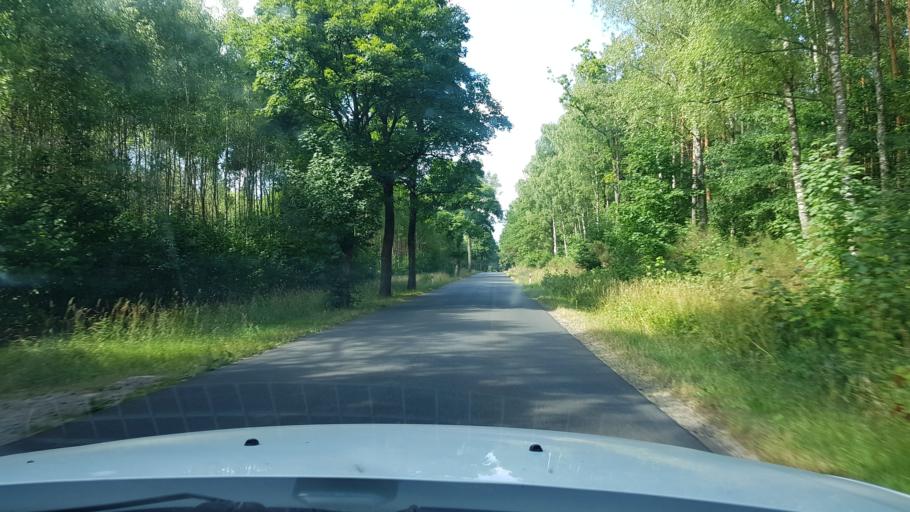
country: PL
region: West Pomeranian Voivodeship
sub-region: Powiat drawski
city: Zlocieniec
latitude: 53.5654
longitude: 16.0102
